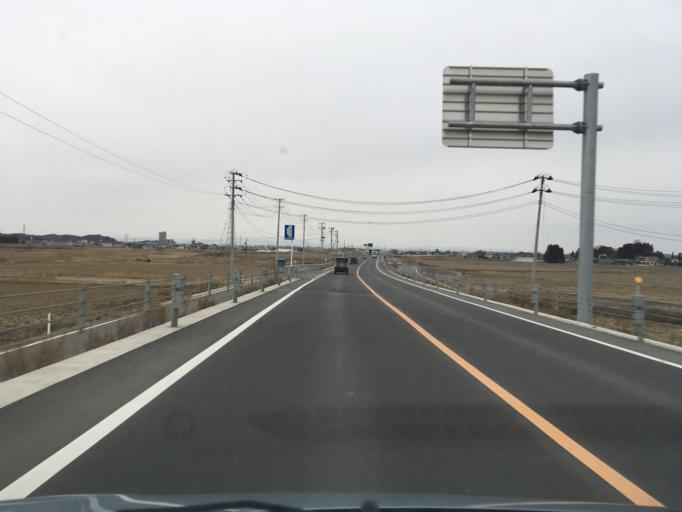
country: JP
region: Miyagi
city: Wakuya
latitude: 38.6901
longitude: 141.2200
